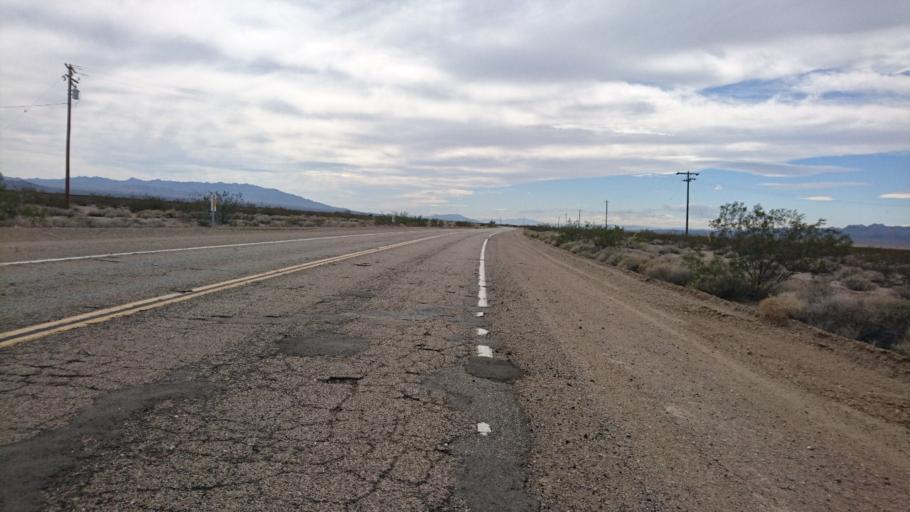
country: US
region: California
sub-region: San Bernardino County
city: Needles
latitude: 34.8041
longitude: -115.1926
